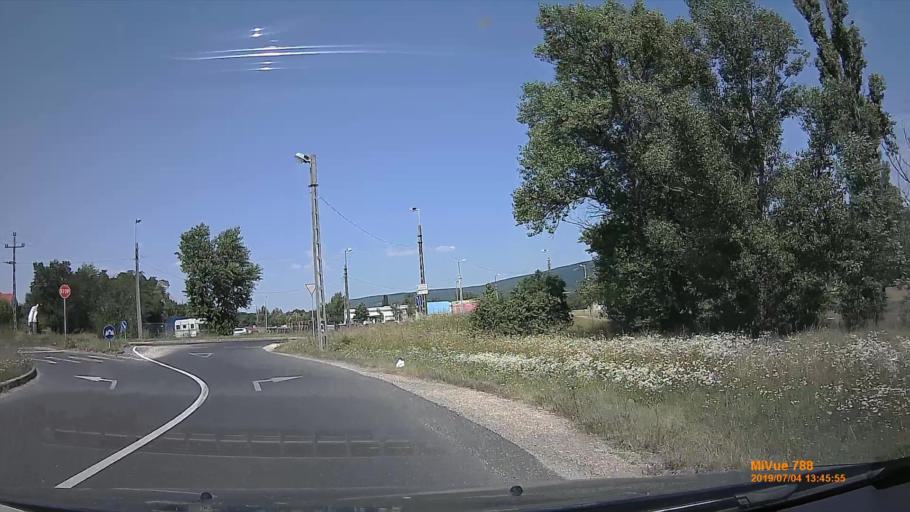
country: HU
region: Komarom-Esztergom
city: Tatabanya
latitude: 47.5823
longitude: 18.3769
